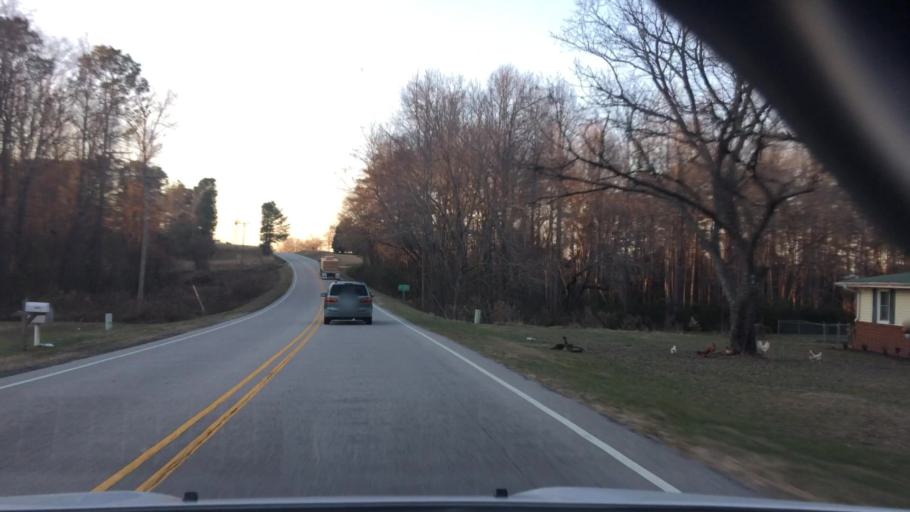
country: US
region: North Carolina
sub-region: Wake County
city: Rolesville
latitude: 35.9415
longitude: -78.4038
